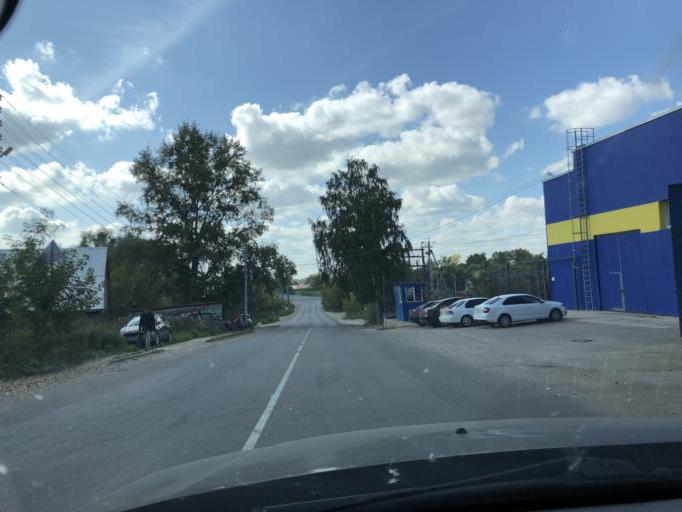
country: RU
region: Tula
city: Yasnogorsk
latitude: 54.4861
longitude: 37.6853
